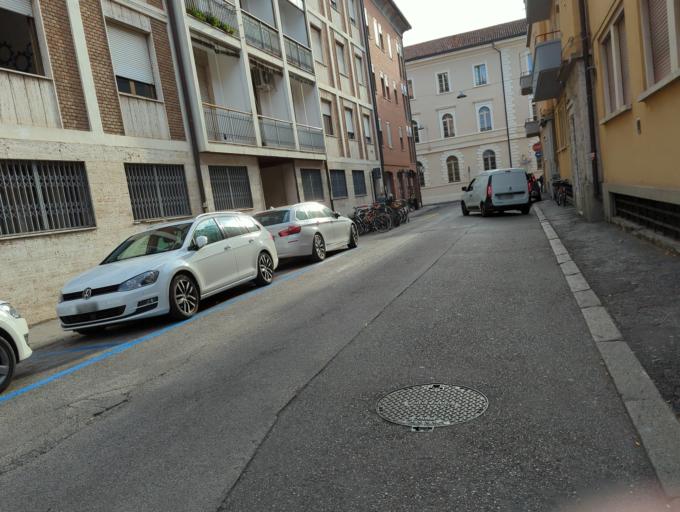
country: IT
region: Emilia-Romagna
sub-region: Provincia di Ferrara
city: Ferrara
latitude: 44.8382
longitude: 11.6226
